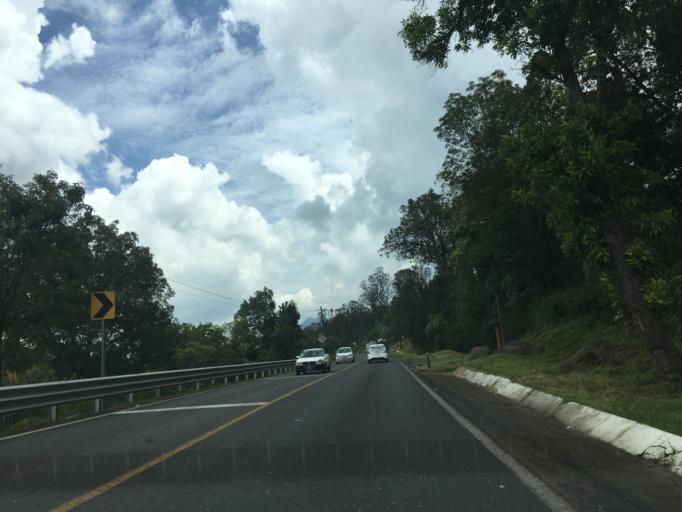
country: MX
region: Michoacan
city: Patzcuaro
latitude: 19.5468
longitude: -101.5929
